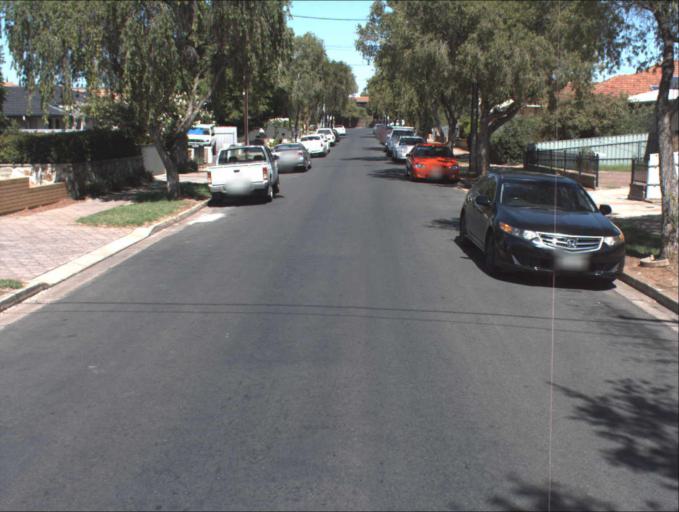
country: AU
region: South Australia
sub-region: Port Adelaide Enfield
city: Klemzig
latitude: -34.8764
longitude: 138.6357
